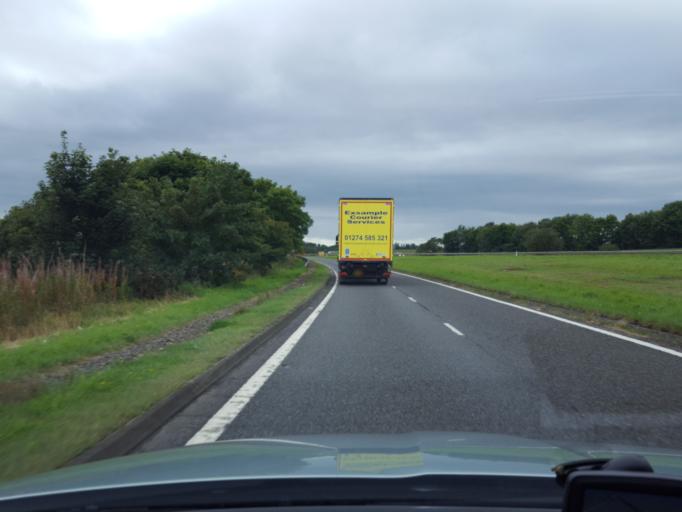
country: GB
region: Scotland
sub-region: Perth and Kinross
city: Milnathort
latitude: 56.2410
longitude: -3.3870
